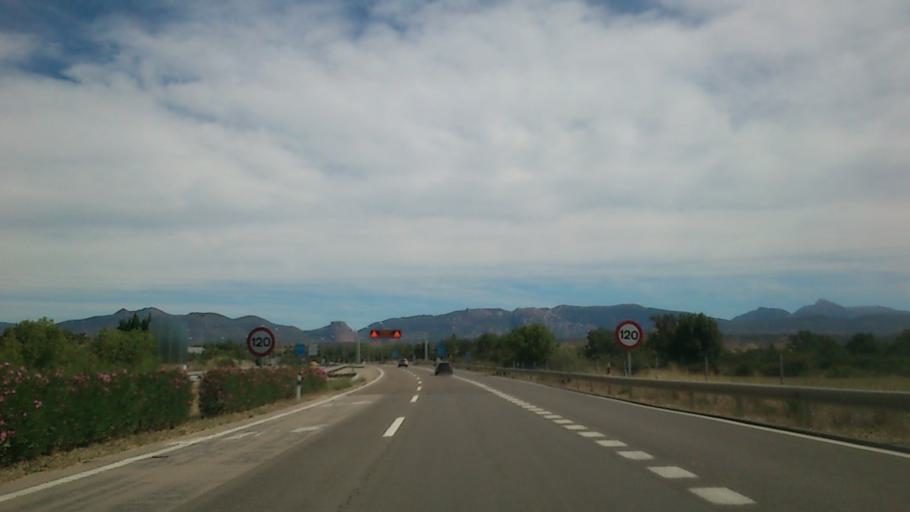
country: ES
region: Aragon
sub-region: Provincia de Huesca
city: Huesca
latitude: 42.1525
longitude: -0.4238
